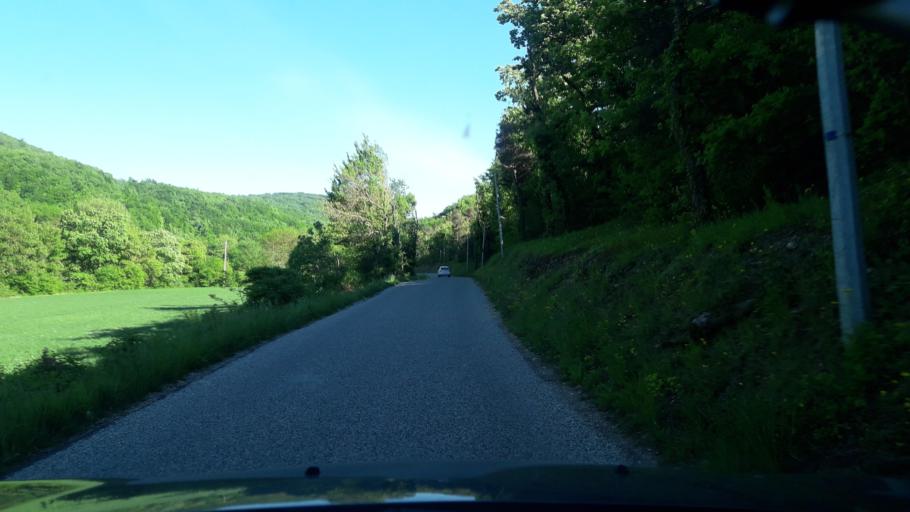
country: FR
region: Rhone-Alpes
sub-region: Departement de la Drome
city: Grane
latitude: 44.7022
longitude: 4.8756
